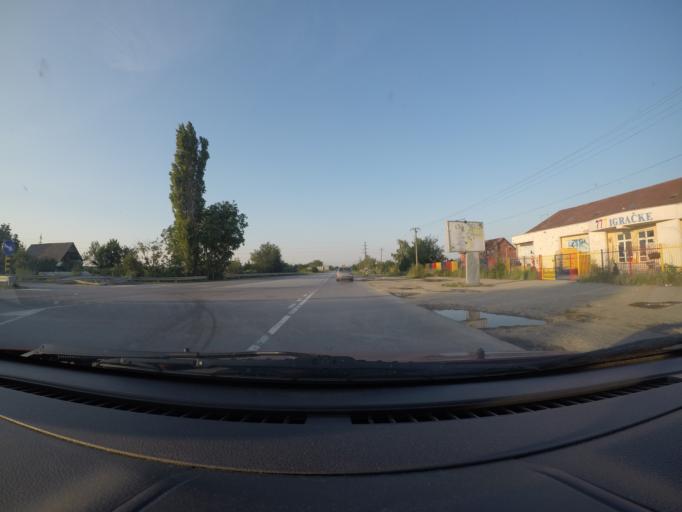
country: RS
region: Central Serbia
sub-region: Podunavski Okrug
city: Smederevo
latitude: 44.5815
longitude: 20.9854
